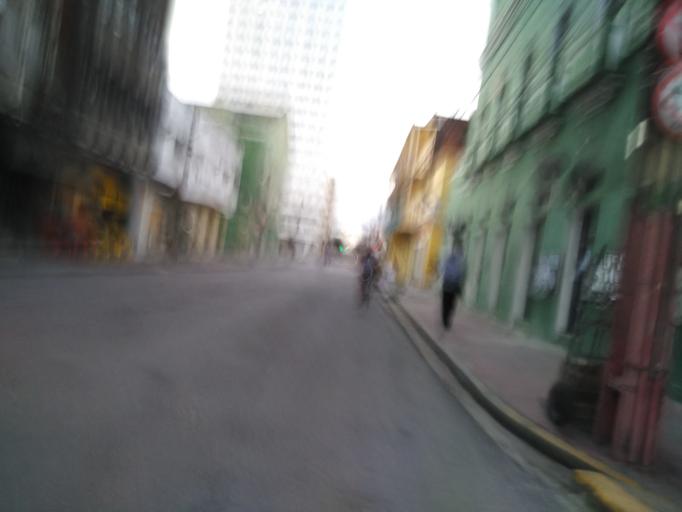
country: BR
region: Pernambuco
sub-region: Recife
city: Recife
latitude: -8.0708
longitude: -34.8815
